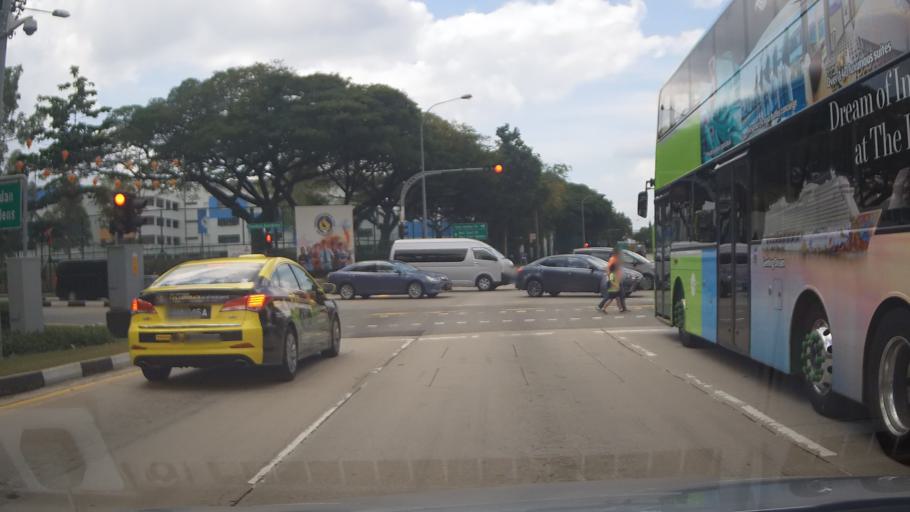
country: SG
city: Singapore
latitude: 1.3217
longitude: 103.7454
